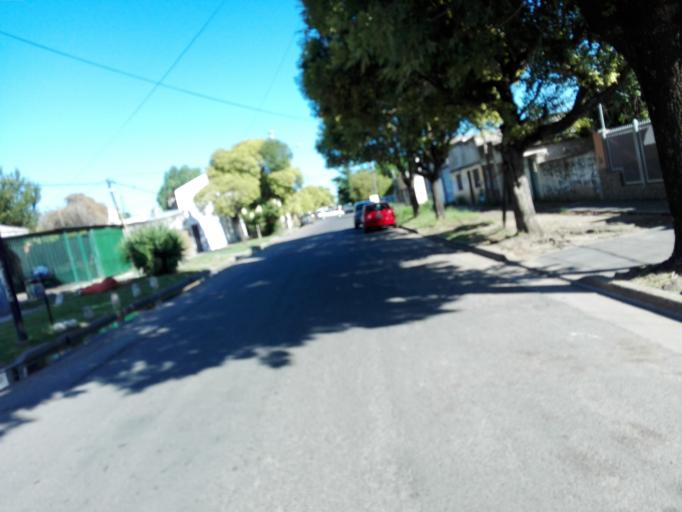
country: AR
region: Buenos Aires
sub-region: Partido de La Plata
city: La Plata
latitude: -34.9510
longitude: -57.9470
